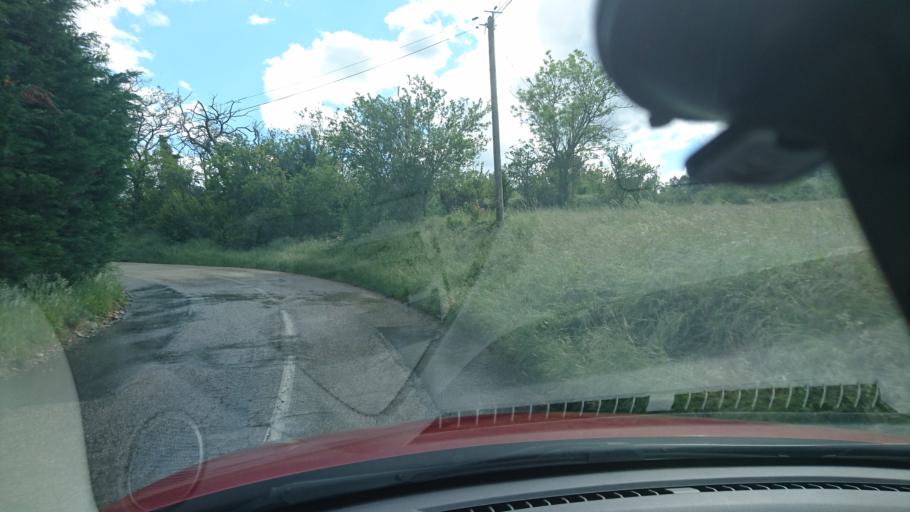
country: FR
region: Rhone-Alpes
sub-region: Departement de la Loire
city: Saint-Pierre-de-Boeuf
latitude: 45.3659
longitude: 4.7307
